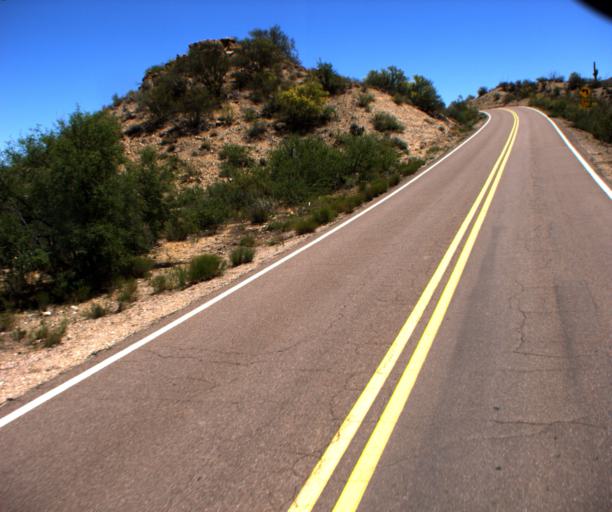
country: US
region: Arizona
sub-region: Yavapai County
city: Bagdad
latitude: 34.4661
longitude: -113.2256
